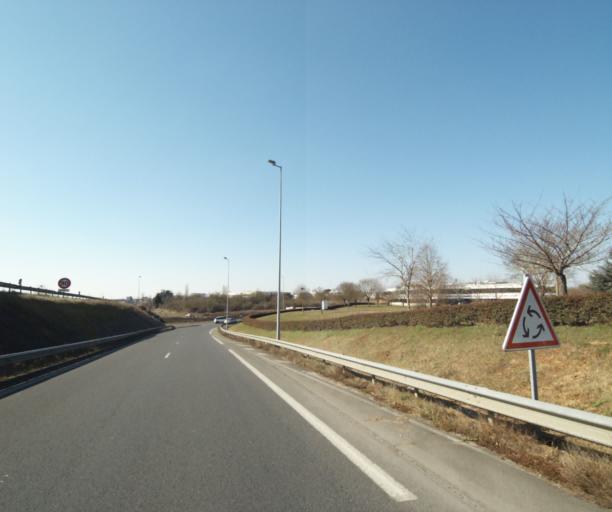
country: FR
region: Poitou-Charentes
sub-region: Departement des Deux-Sevres
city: Chauray
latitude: 46.3396
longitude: -0.4065
